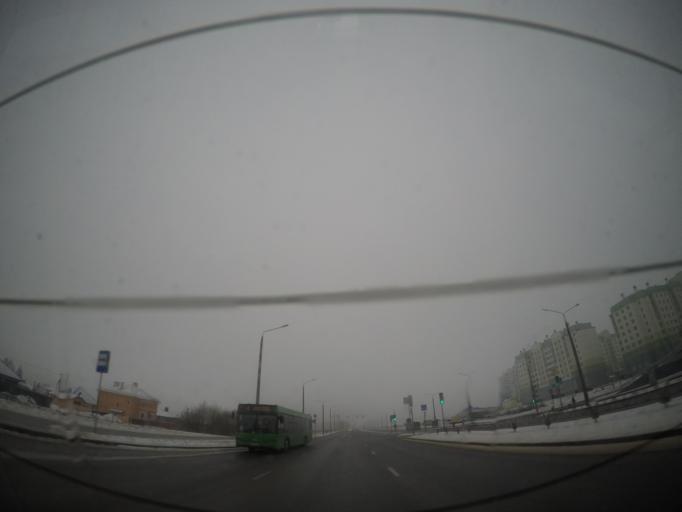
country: BY
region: Grodnenskaya
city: Hrodna
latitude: 53.6152
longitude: 23.8214
